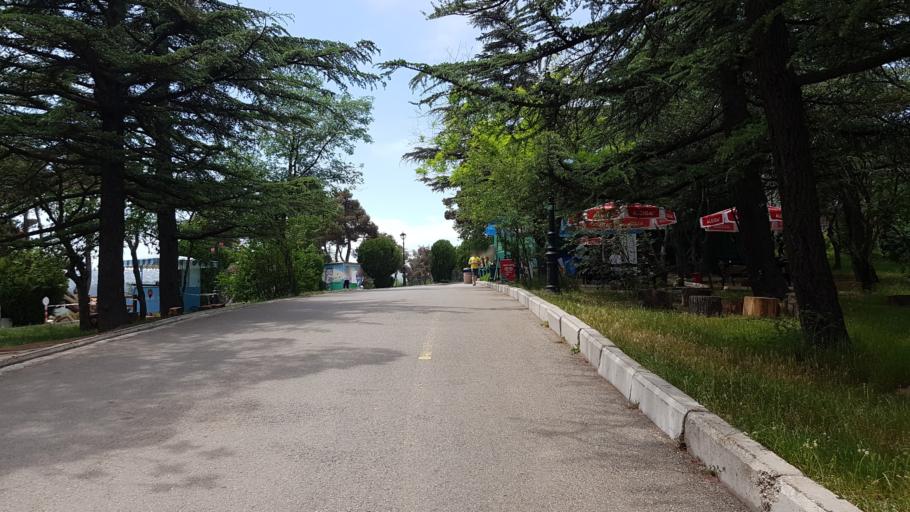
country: GE
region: T'bilisi
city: Tbilisi
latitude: 41.6944
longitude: 44.7829
